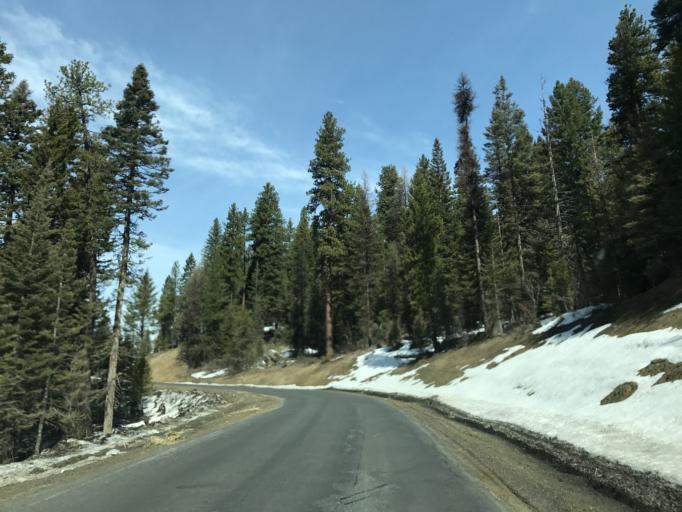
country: US
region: Idaho
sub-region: Valley County
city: McCall
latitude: 44.9767
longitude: -116.1665
